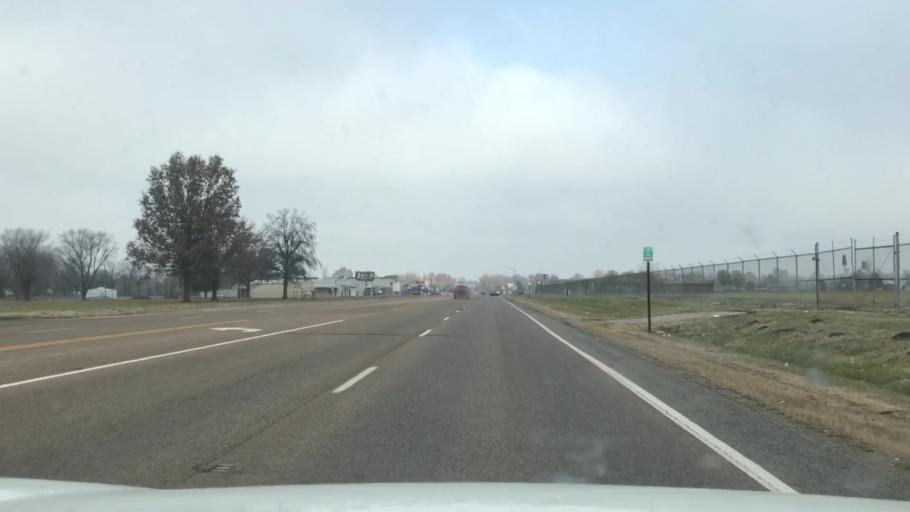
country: US
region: Illinois
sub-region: Madison County
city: Bethalto
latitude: 38.8969
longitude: -90.0593
